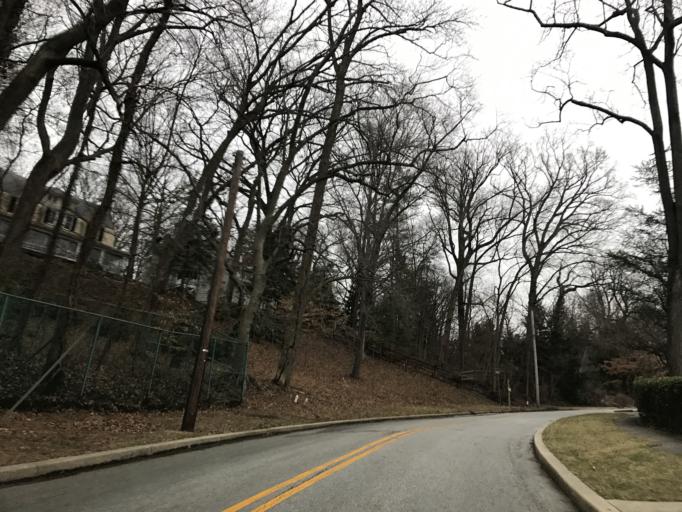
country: US
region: Maryland
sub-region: Baltimore County
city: Towson
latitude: 39.3490
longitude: -76.6398
